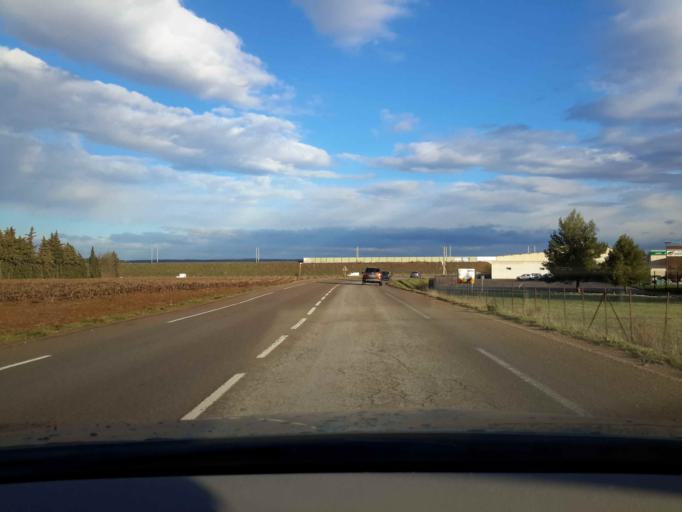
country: FR
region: Languedoc-Roussillon
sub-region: Departement du Gard
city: Generac
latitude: 43.7537
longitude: 4.3421
